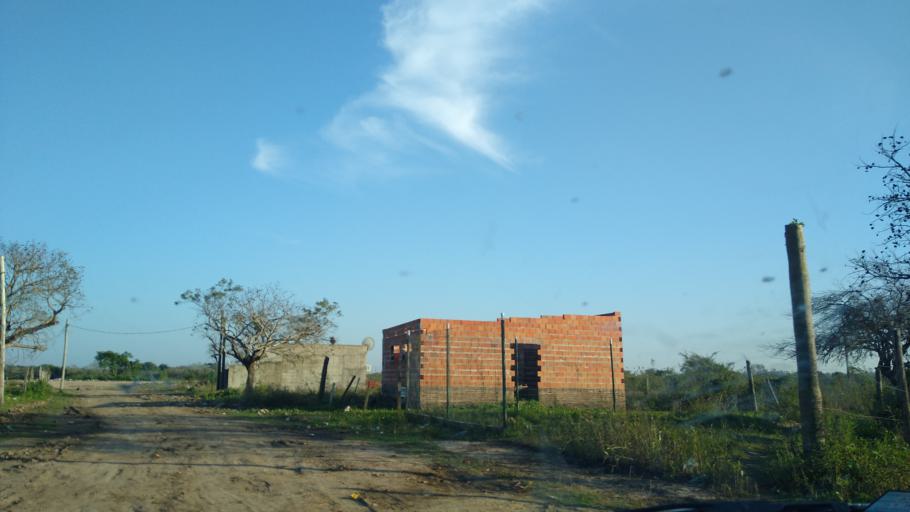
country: AR
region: Chaco
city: Barranqueras
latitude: -27.4653
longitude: -58.9172
